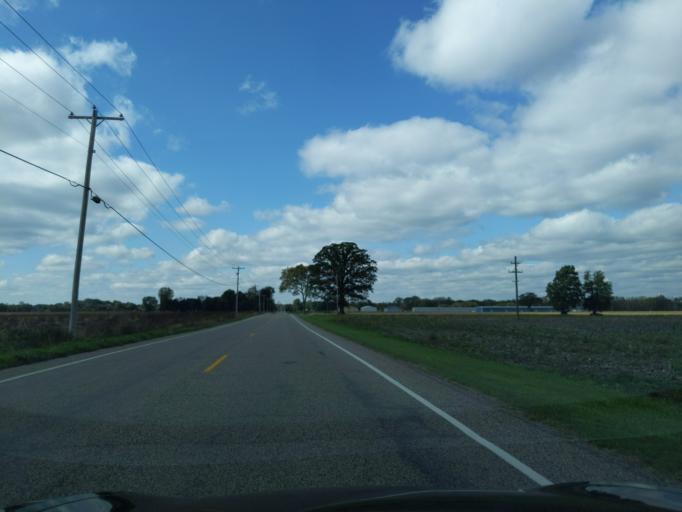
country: US
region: Michigan
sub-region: Eaton County
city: Charlotte
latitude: 42.5676
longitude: -84.8052
